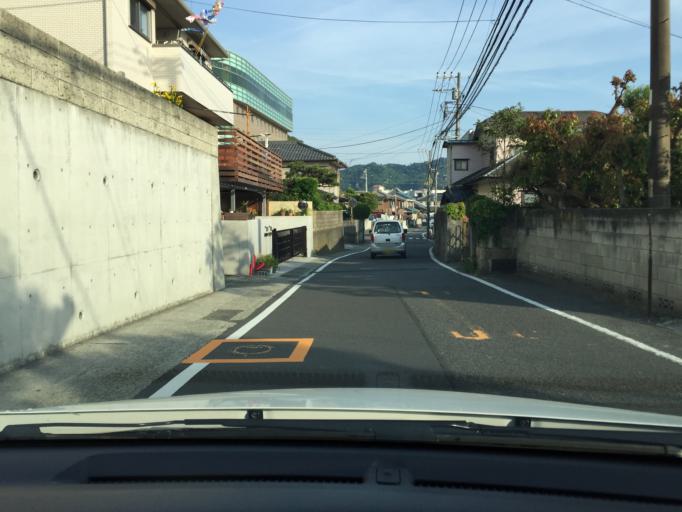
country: JP
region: Kanagawa
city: Hayama
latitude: 35.2811
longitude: 139.5700
